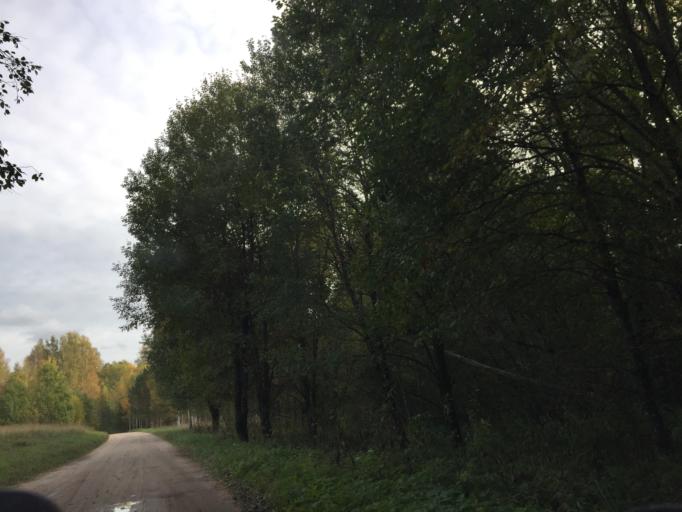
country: LV
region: Jaunpils
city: Jaunpils
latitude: 56.5707
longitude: 23.0259
